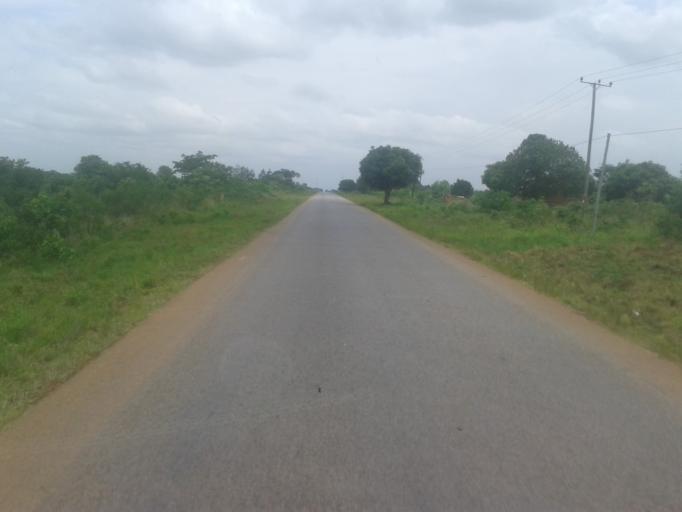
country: UG
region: Western Region
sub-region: Kiryandongo District
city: Masindi Port
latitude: 1.4990
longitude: 32.1274
